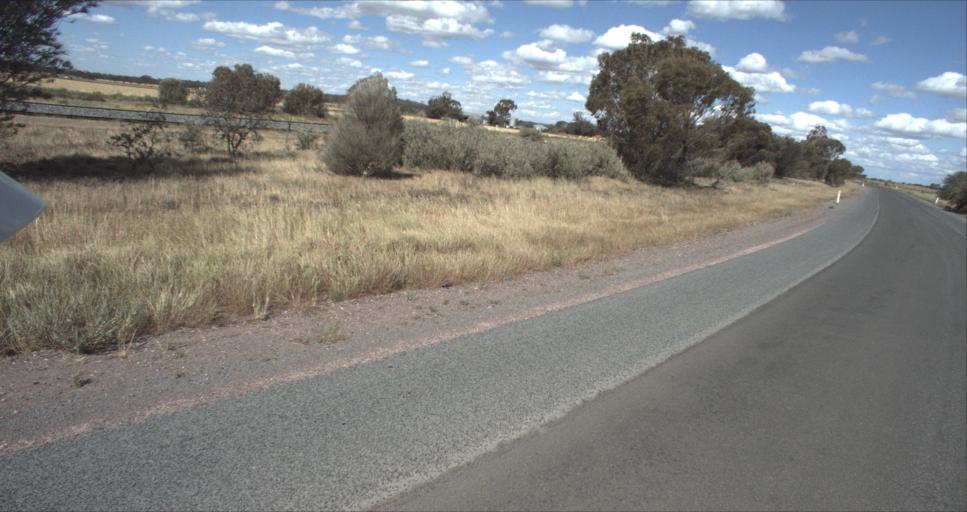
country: AU
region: New South Wales
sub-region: Leeton
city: Leeton
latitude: -34.4233
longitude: 146.2868
